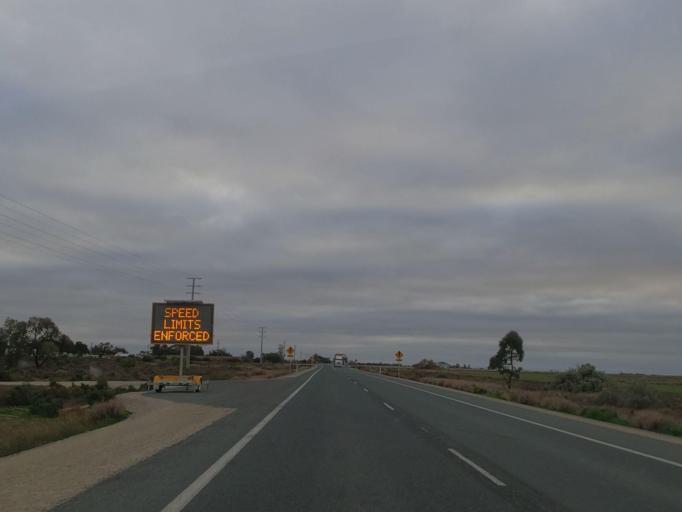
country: AU
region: Victoria
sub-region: Swan Hill
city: Swan Hill
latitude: -35.5541
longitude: 143.7748
